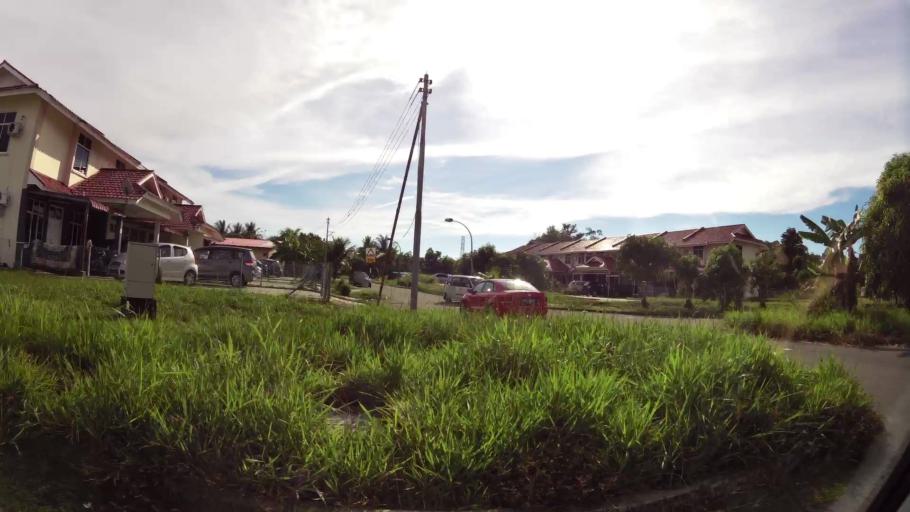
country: BN
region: Brunei and Muara
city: Bandar Seri Begawan
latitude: 4.9746
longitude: 115.0274
